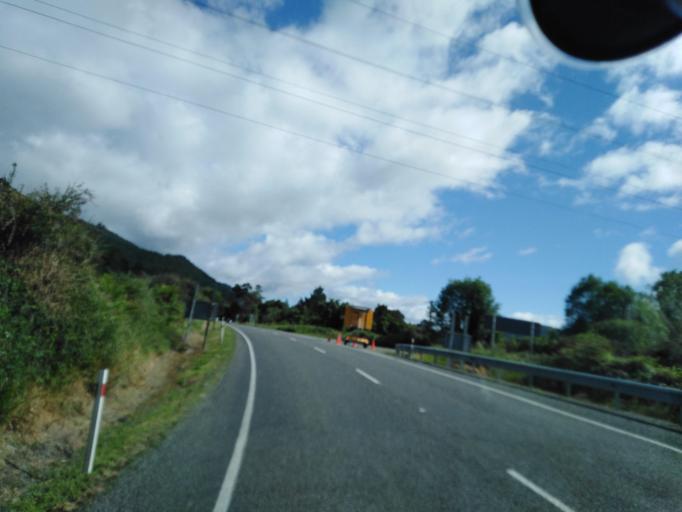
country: NZ
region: Nelson
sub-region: Nelson City
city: Nelson
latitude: -41.2939
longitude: 173.5737
